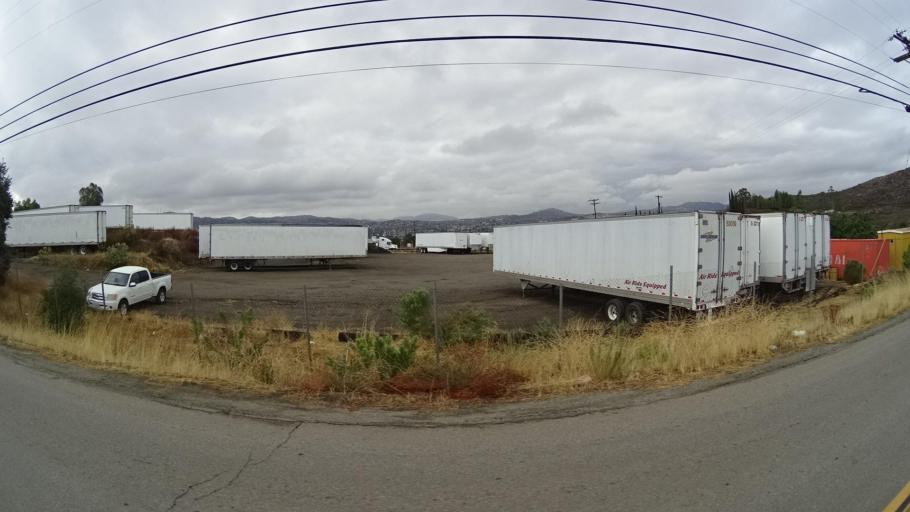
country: MX
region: Baja California
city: Tecate
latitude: 32.5826
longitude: -116.6323
